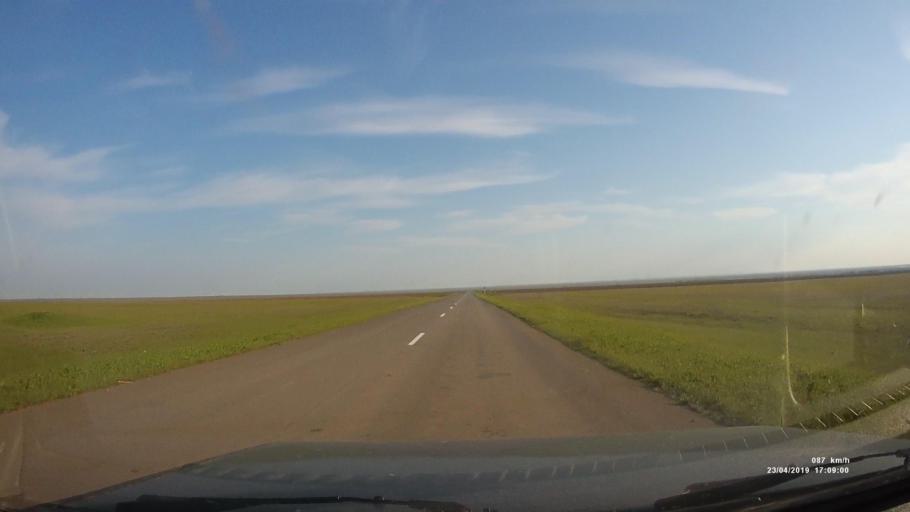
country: RU
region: Kalmykiya
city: Priyutnoye
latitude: 46.2644
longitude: 43.4844
